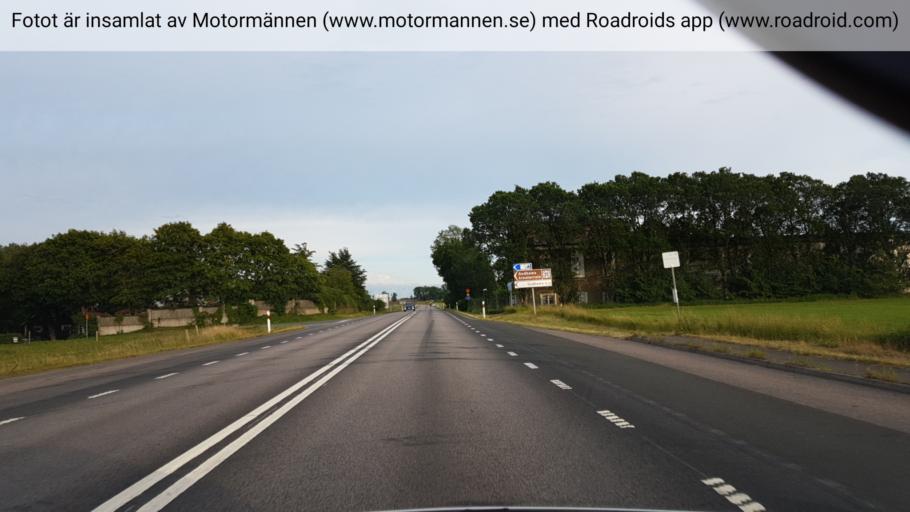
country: SE
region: Vaestra Goetaland
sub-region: Falkopings Kommun
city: Falkoeping
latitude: 58.2357
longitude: 13.5481
